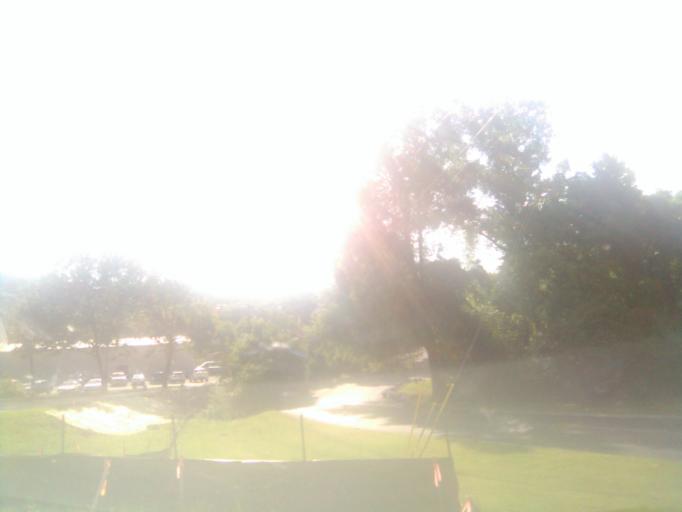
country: US
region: Tennessee
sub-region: Davidson County
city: Belle Meade
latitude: 36.0796
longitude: -86.8855
